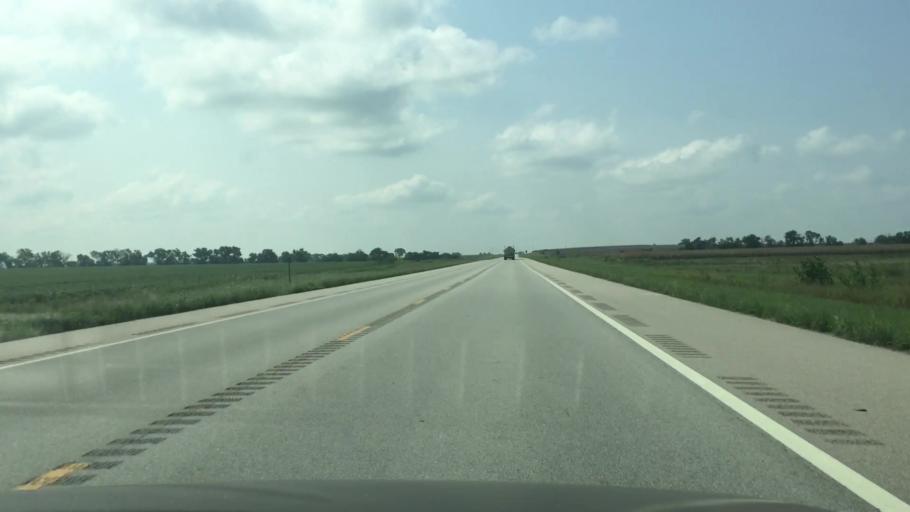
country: US
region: Kansas
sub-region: Allen County
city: Iola
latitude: 37.9638
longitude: -95.3812
